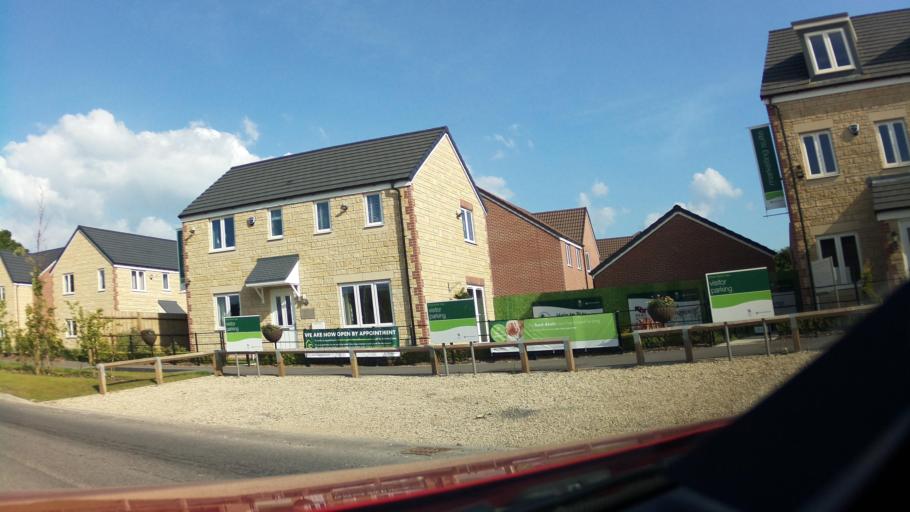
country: GB
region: England
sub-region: Wiltshire
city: Chippenham
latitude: 51.4741
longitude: -2.1138
